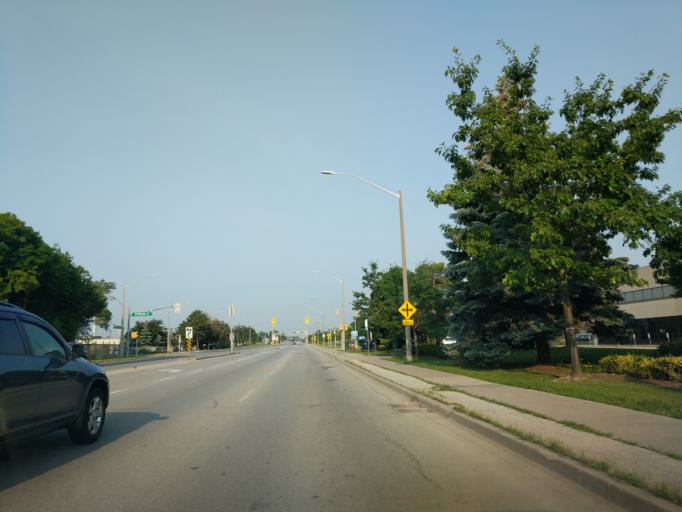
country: CA
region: Ontario
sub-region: York
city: Richmond Hill
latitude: 43.8921
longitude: -79.4303
